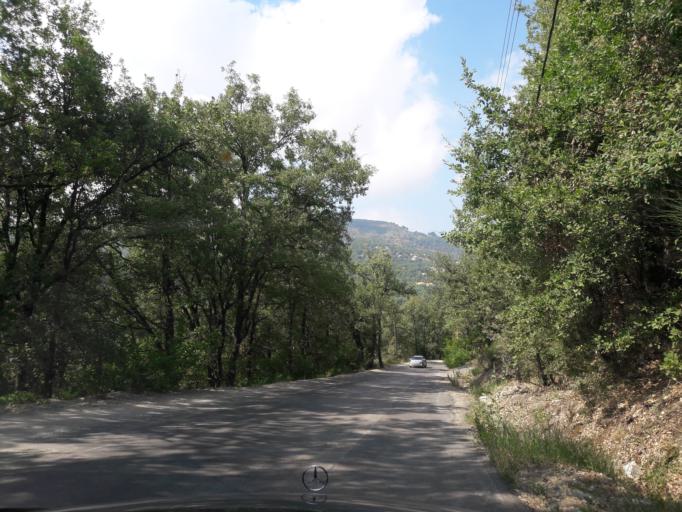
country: LB
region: Mont-Liban
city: Djounie
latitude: 33.9583
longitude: 35.7769
